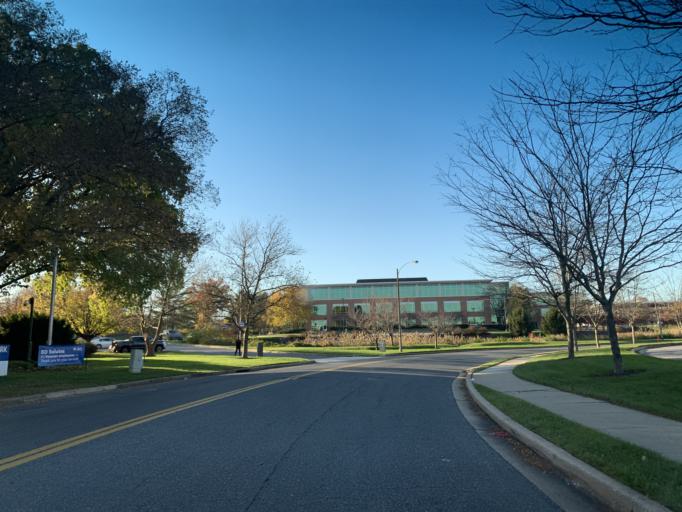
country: US
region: Maryland
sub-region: Baltimore County
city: Cockeysville
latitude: 39.4893
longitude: -76.6637
